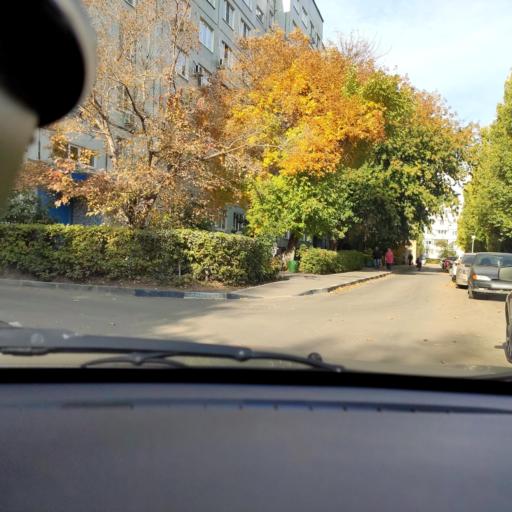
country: RU
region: Samara
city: Tol'yatti
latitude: 53.5313
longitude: 49.3202
